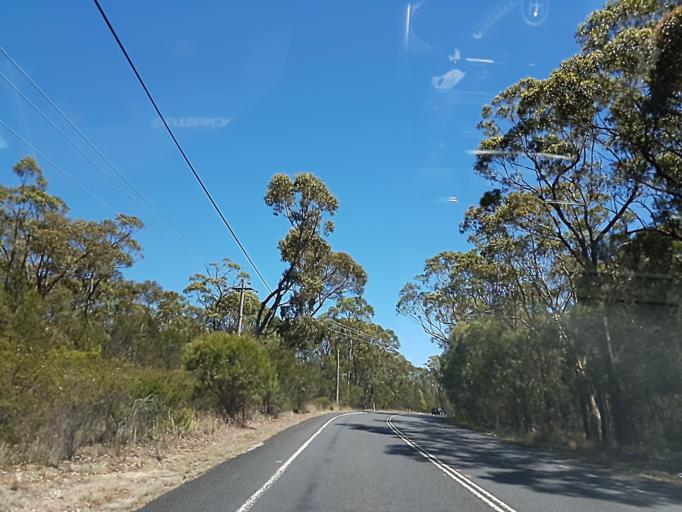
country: AU
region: New South Wales
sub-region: Hornsby Shire
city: Glenorie
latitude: -33.5147
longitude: 151.0277
